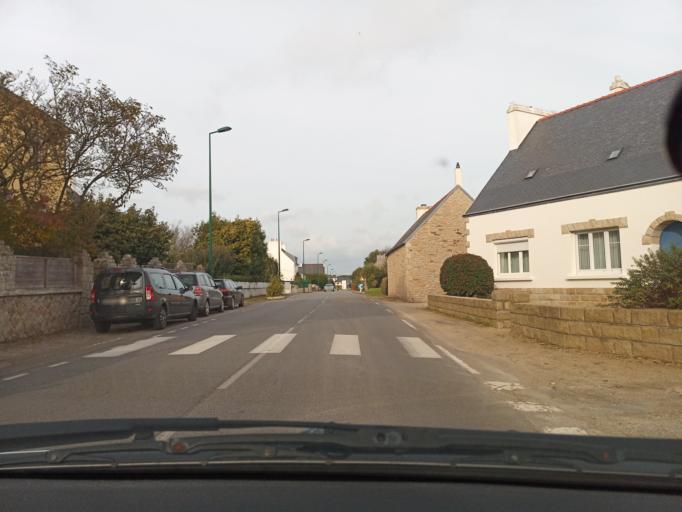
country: FR
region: Brittany
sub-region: Departement du Finistere
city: Plozevet
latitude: 47.9898
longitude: -4.4218
